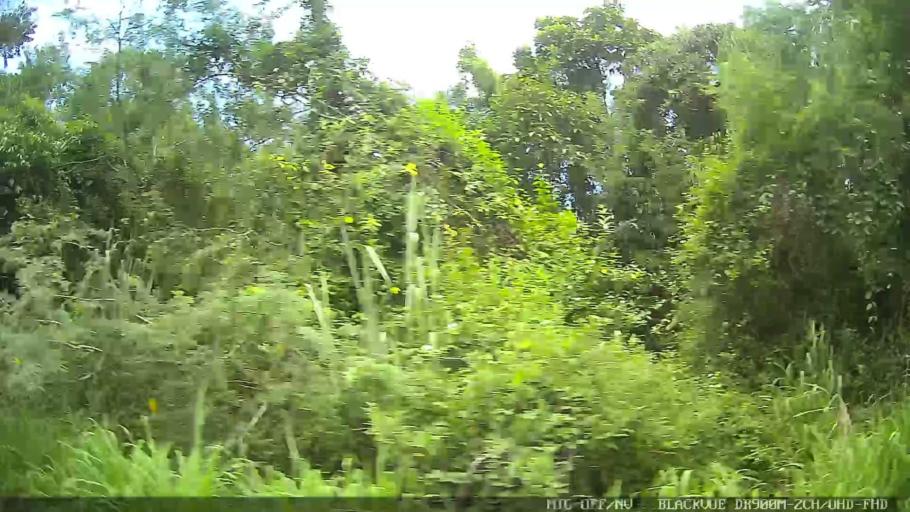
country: BR
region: Sao Paulo
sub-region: Iguape
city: Iguape
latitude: -24.6967
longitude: -47.5339
